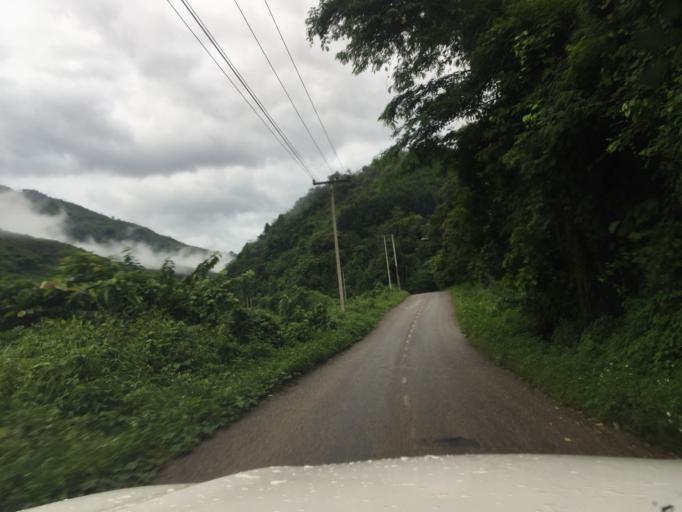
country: LA
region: Oudomxai
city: Muang La
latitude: 21.0107
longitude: 102.2336
